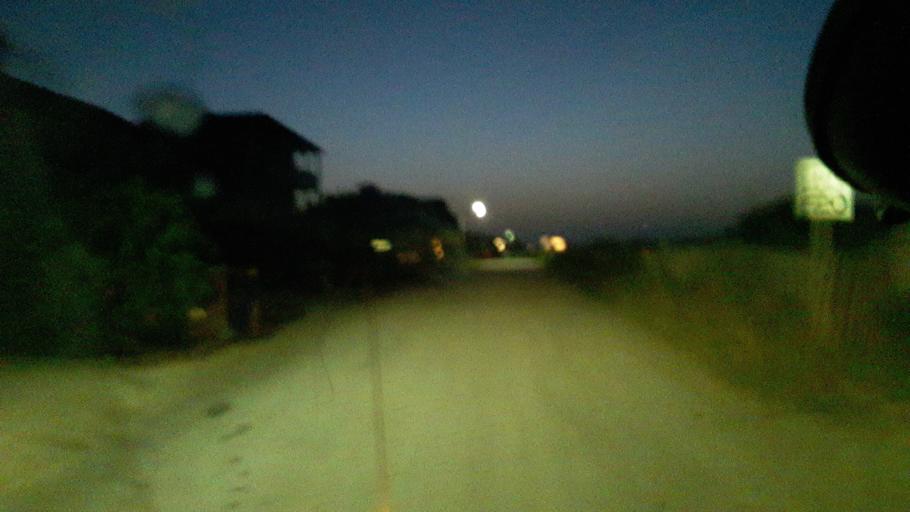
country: US
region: North Carolina
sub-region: Brunswick County
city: Shallotte
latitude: 33.8956
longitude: -78.4041
